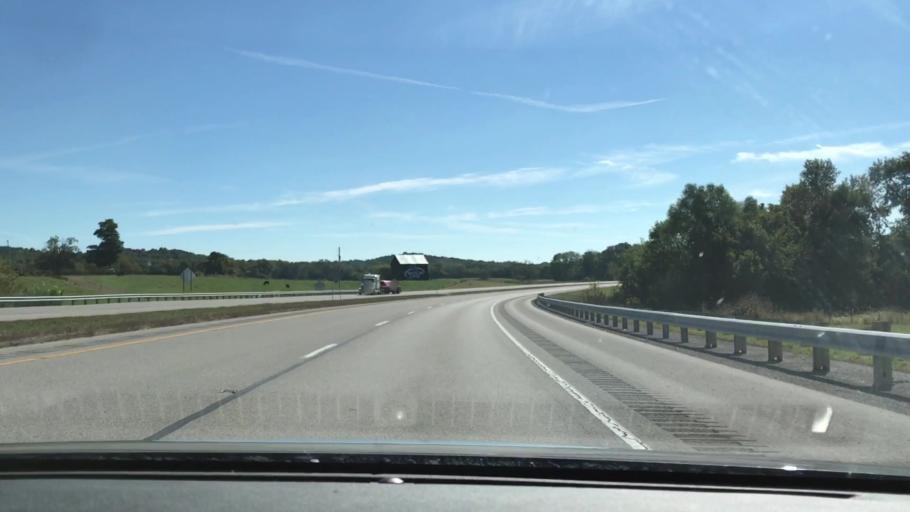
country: US
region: Kentucky
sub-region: Todd County
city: Elkton
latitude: 36.8235
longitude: -87.1490
